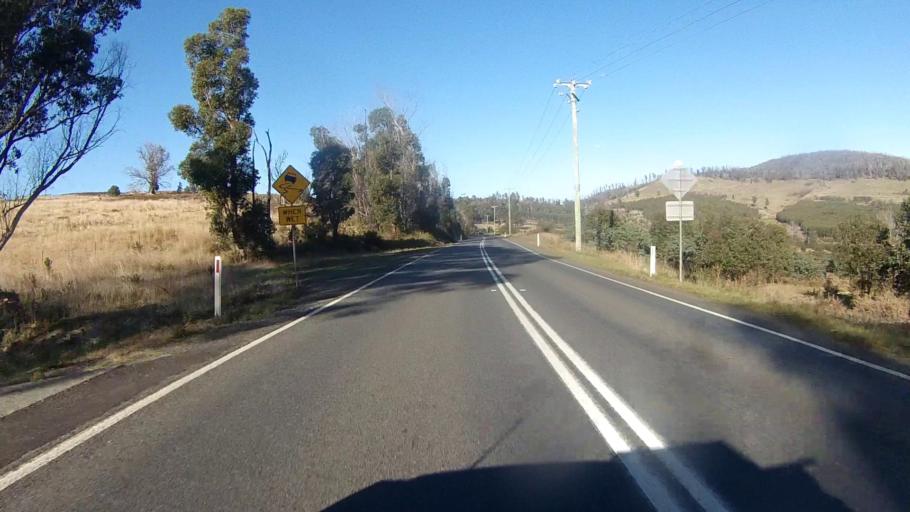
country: AU
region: Tasmania
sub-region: Sorell
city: Sorell
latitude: -42.8342
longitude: 147.8066
